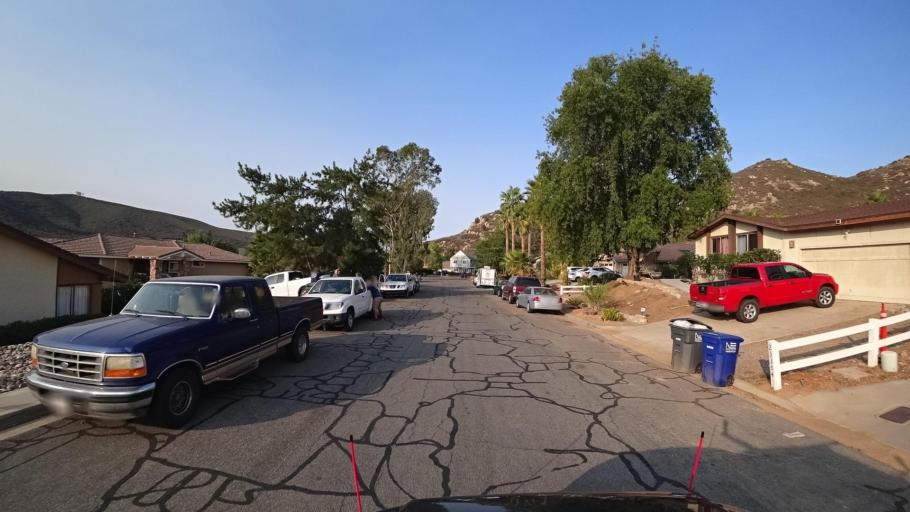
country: US
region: California
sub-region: San Diego County
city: San Diego Country Estates
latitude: 33.0055
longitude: -116.8259
